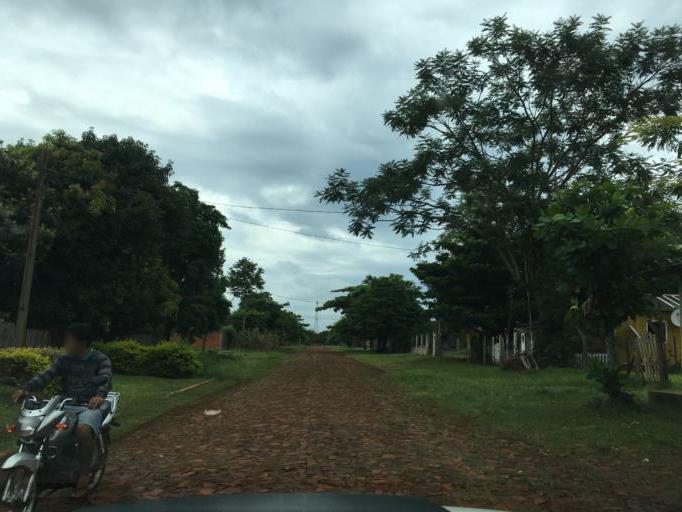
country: PY
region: Alto Parana
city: Ciudad del Este
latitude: -25.4138
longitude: -54.6538
